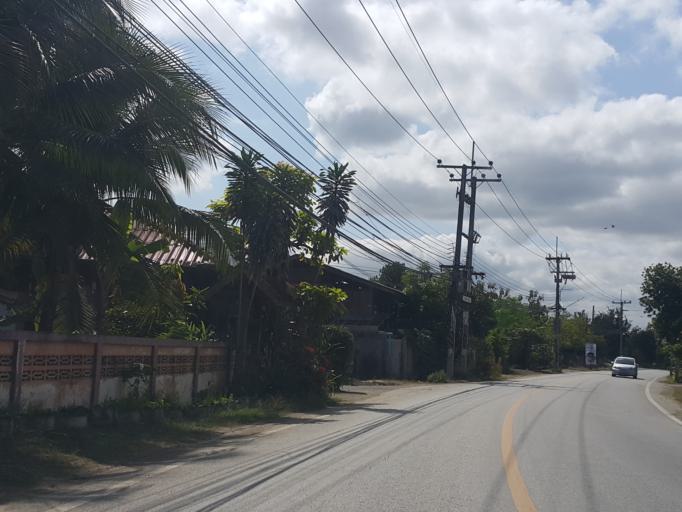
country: TH
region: Lamphun
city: Ban Thi
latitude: 18.6678
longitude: 99.1359
